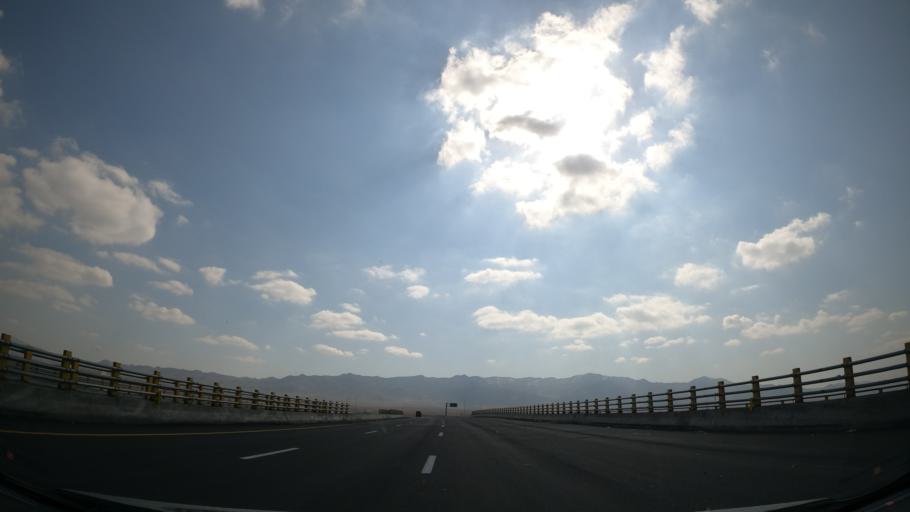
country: IR
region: Alborz
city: Eshtehard
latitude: 35.7323
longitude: 50.5609
